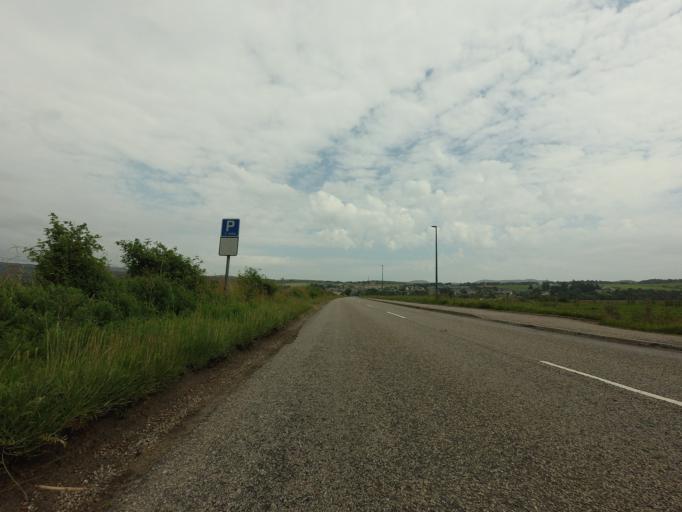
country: GB
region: Scotland
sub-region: Highland
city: Alness
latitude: 57.8876
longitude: -4.3570
